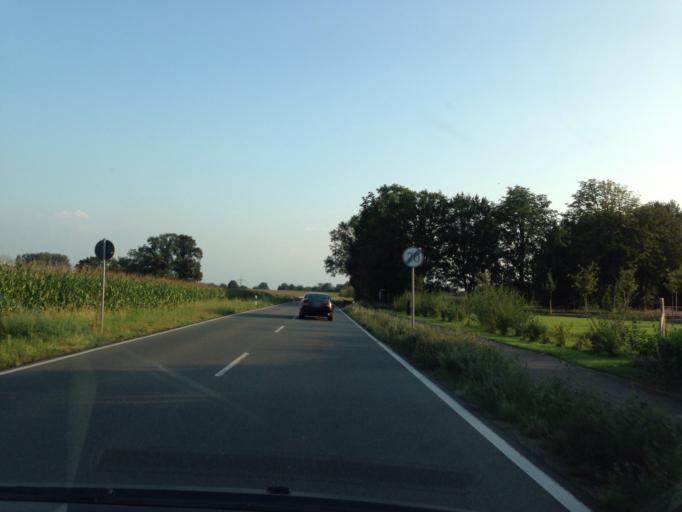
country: DE
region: North Rhine-Westphalia
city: Ludinghausen
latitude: 51.7484
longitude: 7.4245
